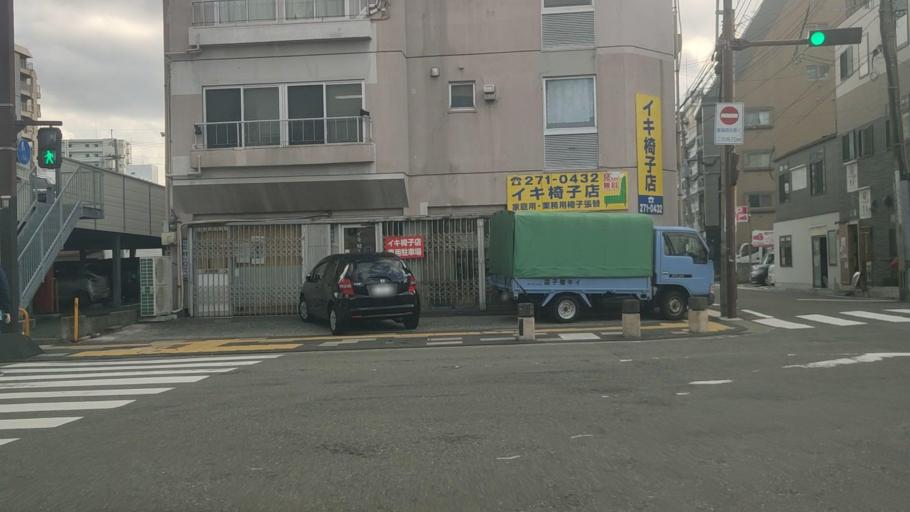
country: JP
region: Fukuoka
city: Fukuoka-shi
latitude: 33.5880
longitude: 130.4106
